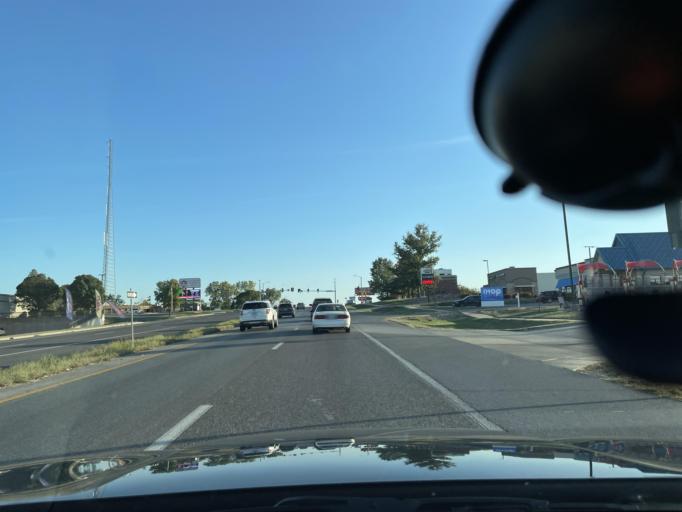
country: US
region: Missouri
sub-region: Andrew County
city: Country Club Village
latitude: 39.8047
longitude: -94.8153
